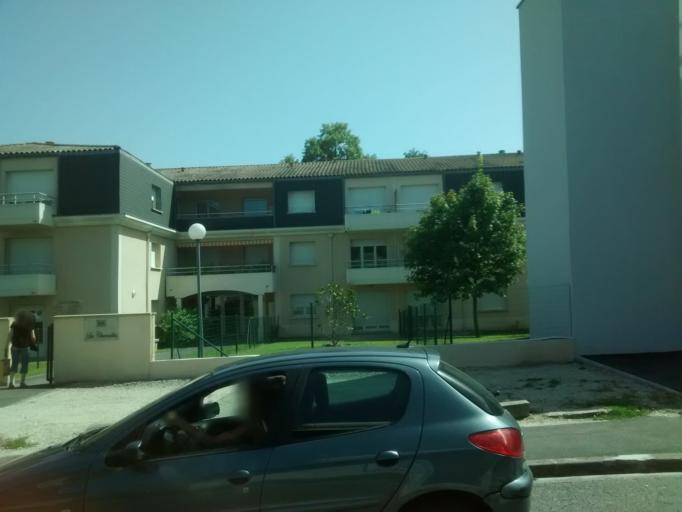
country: FR
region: Aquitaine
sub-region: Departement de la Gironde
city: Merignac
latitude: 44.8406
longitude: -0.6408
